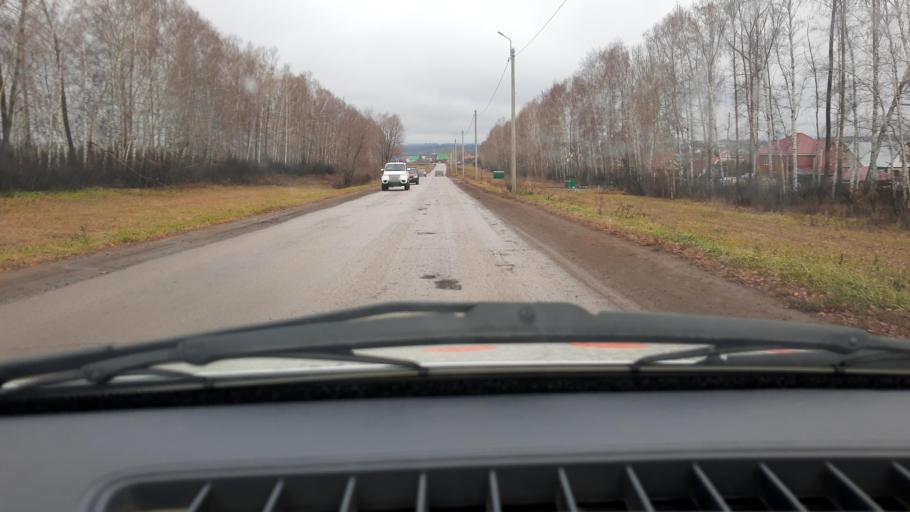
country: RU
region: Bashkortostan
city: Iglino
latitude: 54.8019
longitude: 56.3801
